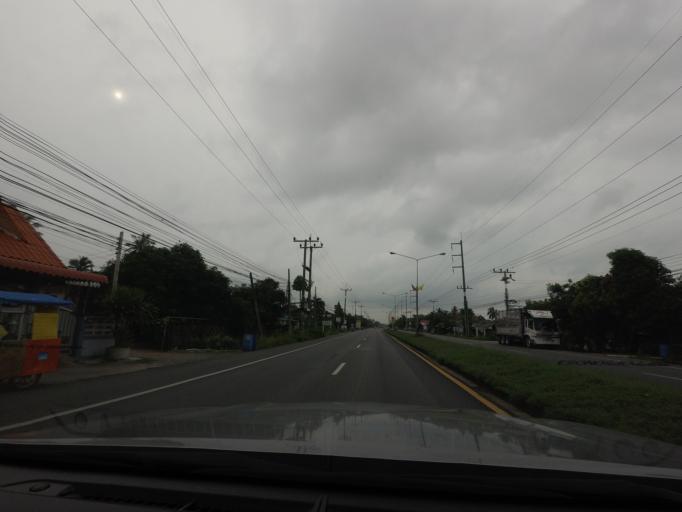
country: TH
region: Songkhla
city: Sathing Phra
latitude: 7.3955
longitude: 100.4664
